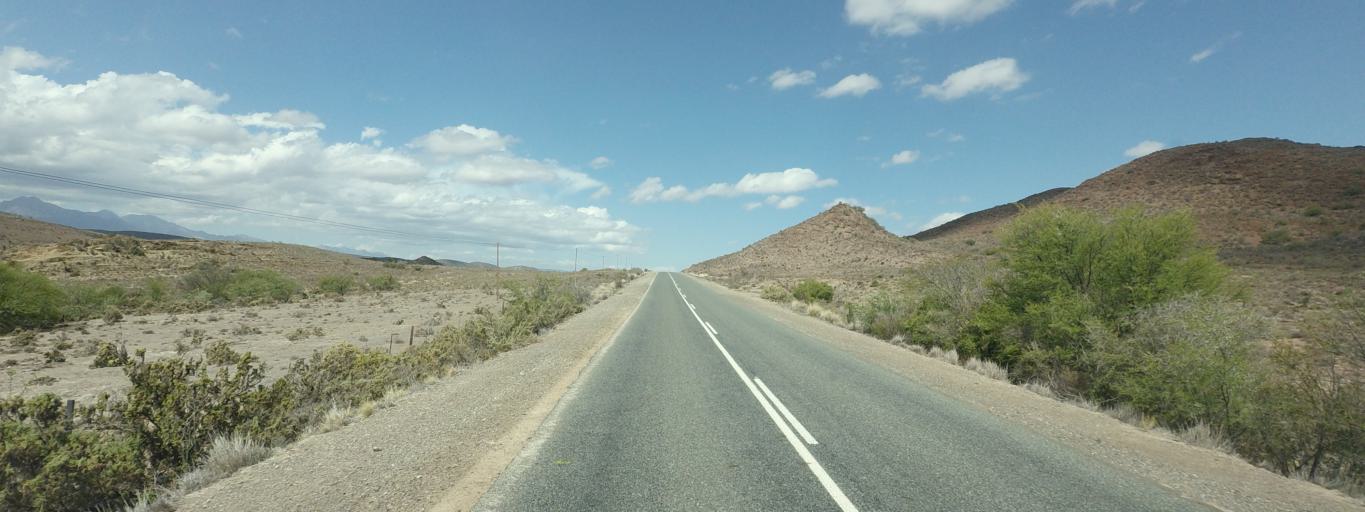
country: ZA
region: Western Cape
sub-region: Eden District Municipality
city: Ladismith
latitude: -33.5995
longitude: 21.1102
